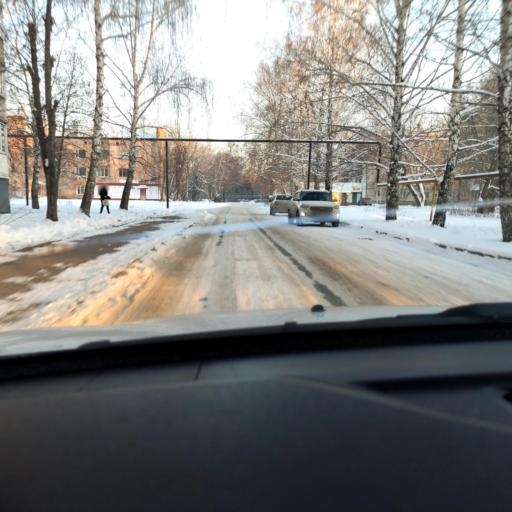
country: RU
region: Samara
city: Smyshlyayevka
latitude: 53.2513
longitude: 50.3757
